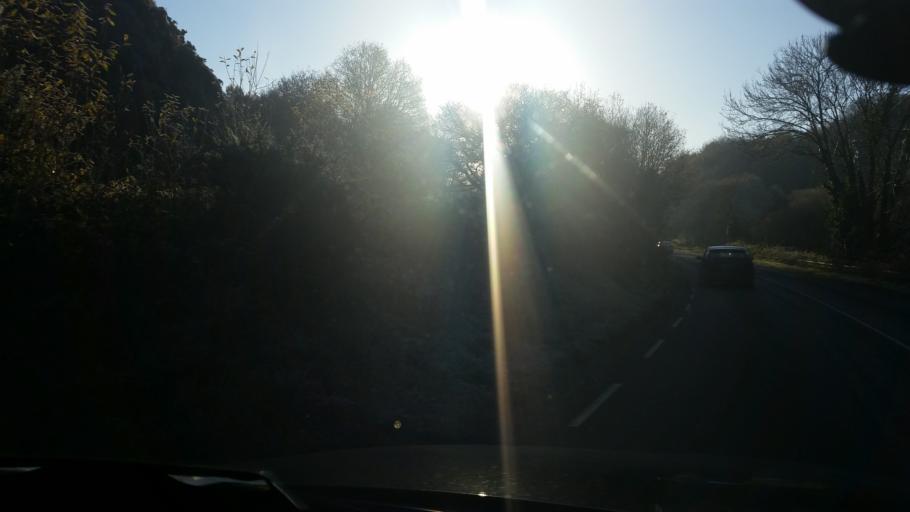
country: IE
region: Leinster
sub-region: Loch Garman
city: Gorey
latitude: 52.6504
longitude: -6.2919
